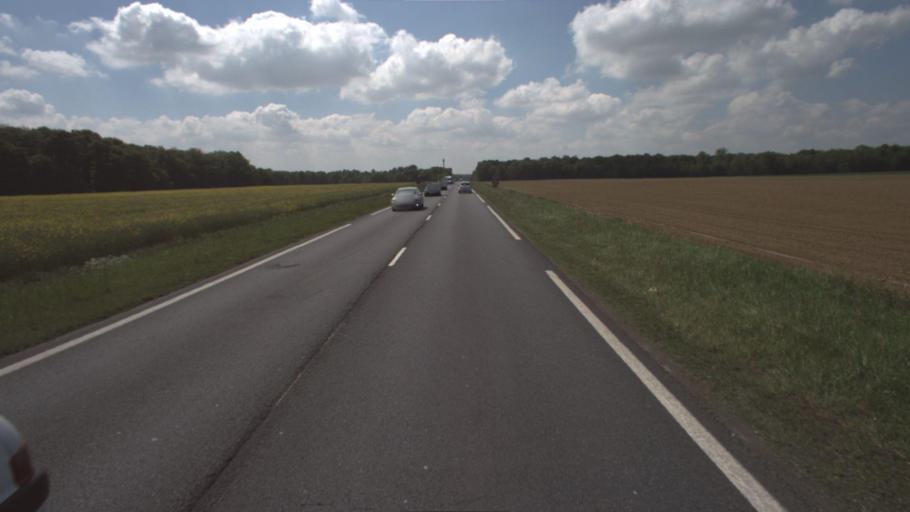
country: FR
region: Ile-de-France
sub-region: Departement de Seine-et-Marne
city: Chaumes-en-Brie
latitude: 48.6747
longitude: 2.8131
